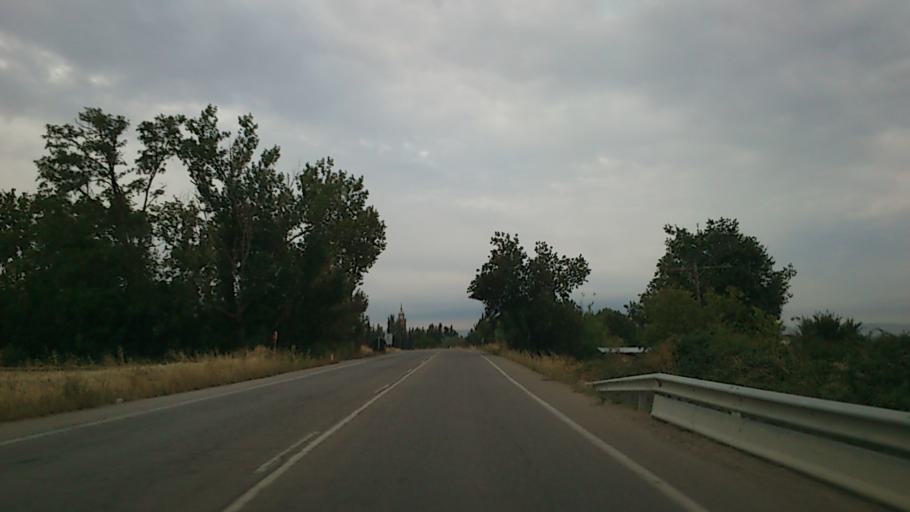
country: ES
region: Aragon
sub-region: Provincia de Zaragoza
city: Villanueva de Gallego
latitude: 41.7294
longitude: -0.8092
